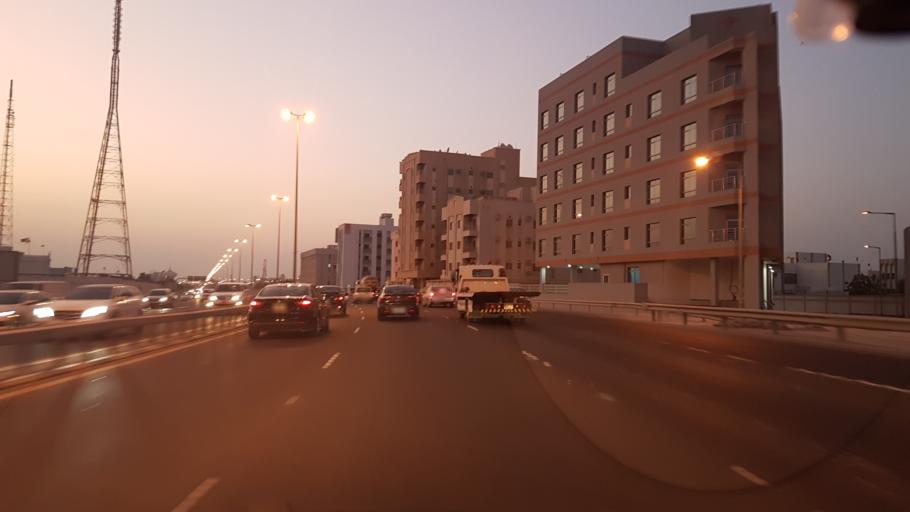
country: BH
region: Northern
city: Madinat `Isa
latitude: 26.1624
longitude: 50.5612
